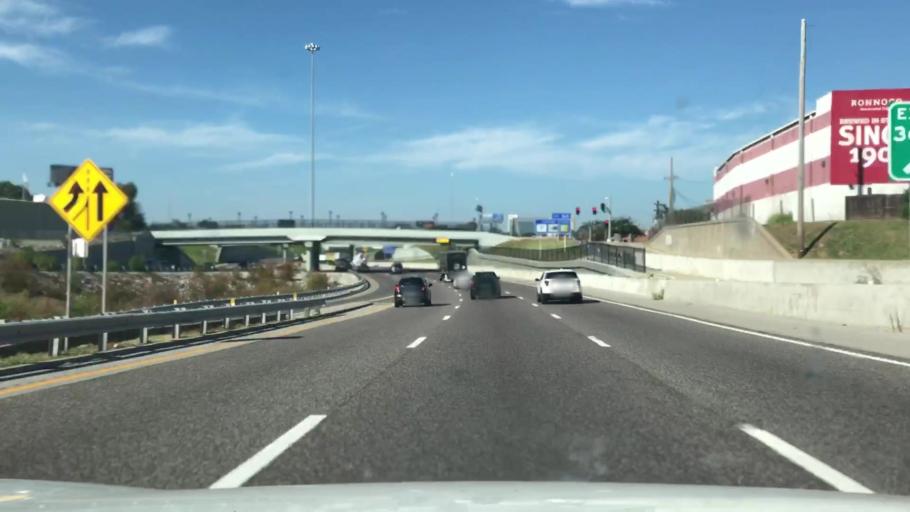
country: US
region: Missouri
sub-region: City of Saint Louis
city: St. Louis
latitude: 38.6313
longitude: -90.2516
